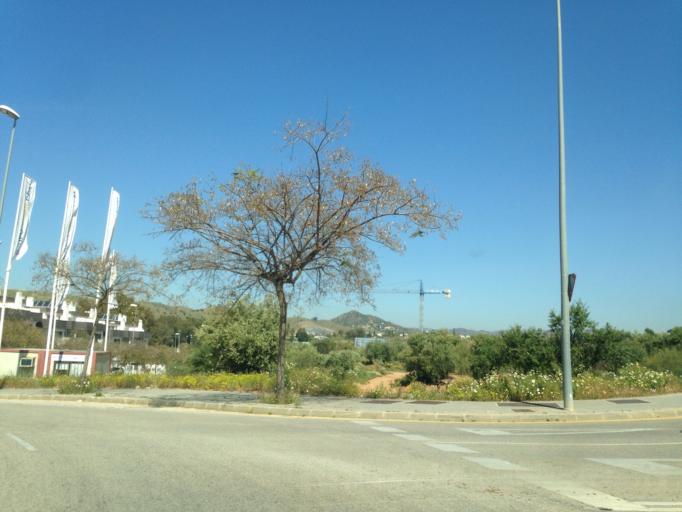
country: ES
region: Andalusia
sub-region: Provincia de Malaga
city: Malaga
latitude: 36.7325
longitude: -4.4892
